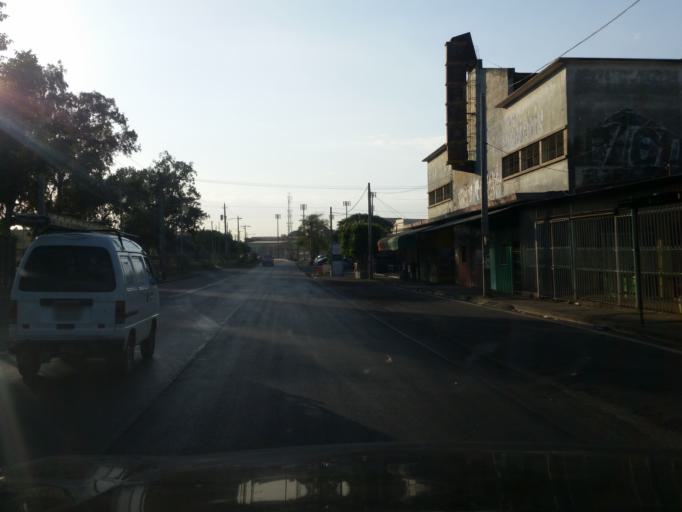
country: NI
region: Managua
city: Managua
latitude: 12.1543
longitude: -86.2665
